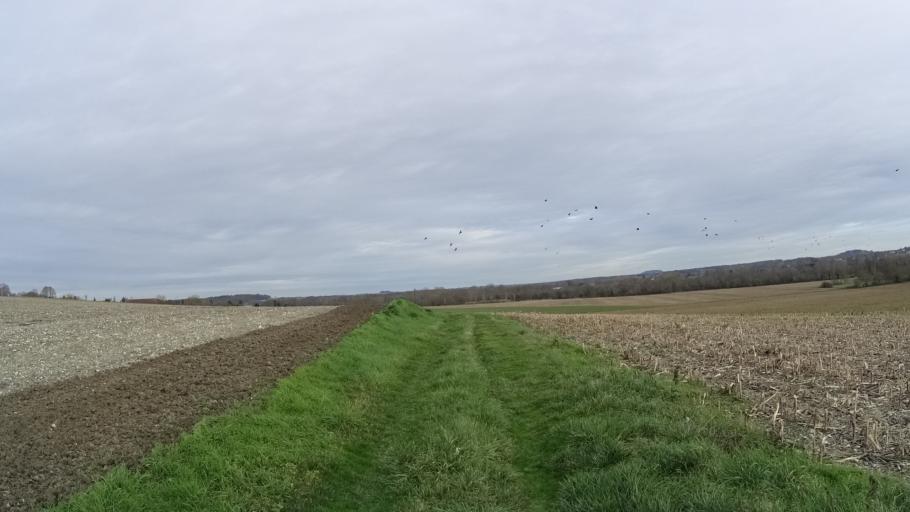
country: FR
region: Aquitaine
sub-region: Departement de la Dordogne
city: Saint-Aulaye
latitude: 45.2586
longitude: 0.1657
